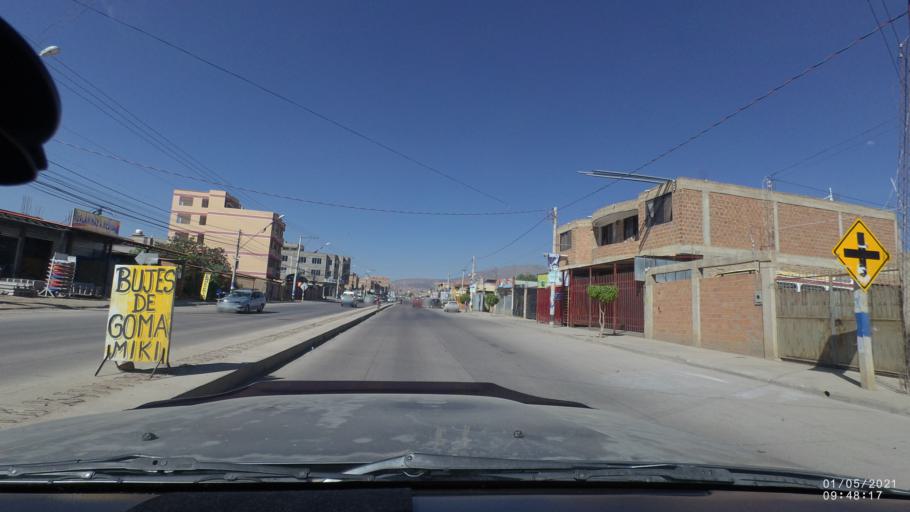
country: BO
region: Cochabamba
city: Cochabamba
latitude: -17.4525
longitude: -66.1667
